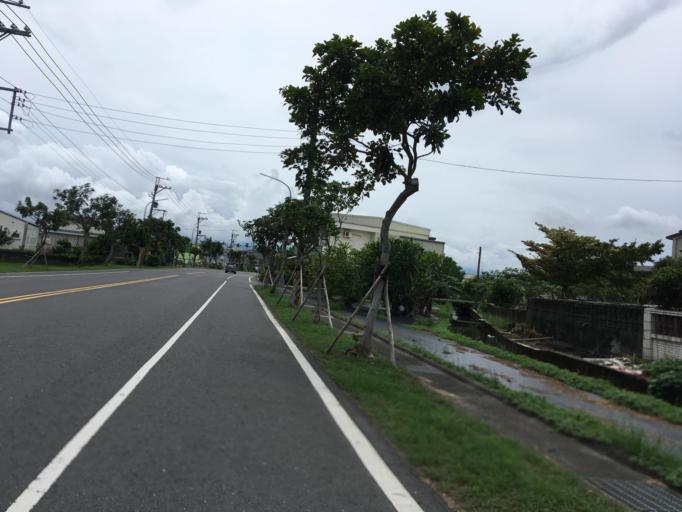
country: TW
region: Taiwan
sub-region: Yilan
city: Yilan
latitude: 24.6908
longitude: 121.8064
